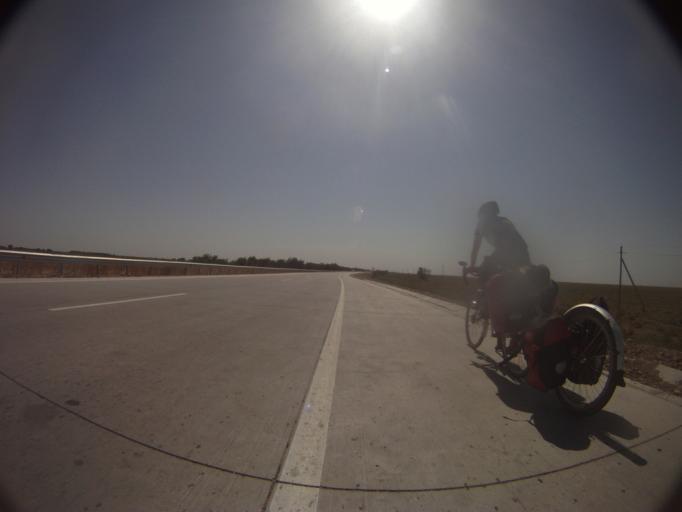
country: KZ
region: Ongtustik Qazaqstan
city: Bayaldyr
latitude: 43.1211
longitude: 68.6022
